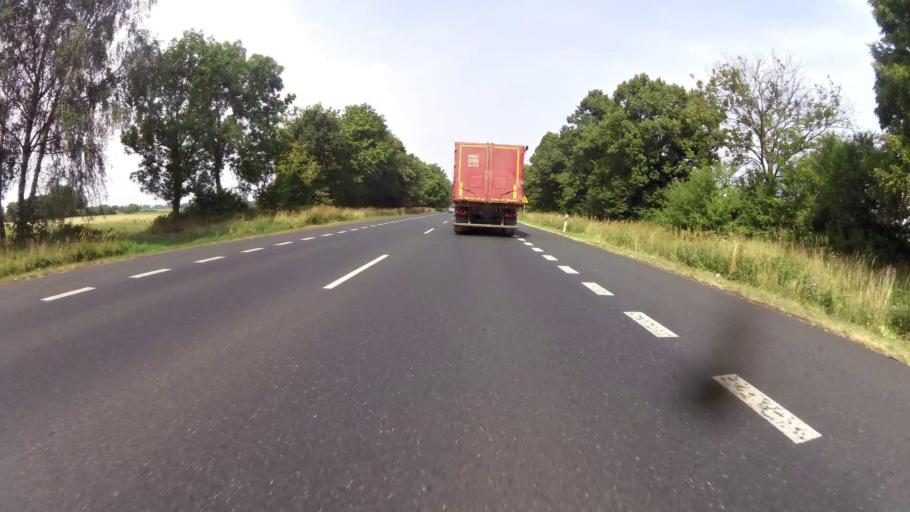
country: PL
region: West Pomeranian Voivodeship
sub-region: Powiat pyrzycki
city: Lipiany
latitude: 52.9690
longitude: 14.9706
